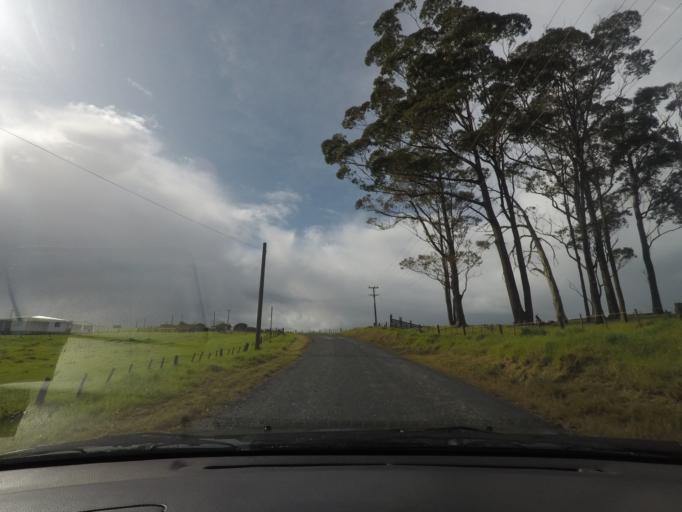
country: NZ
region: Auckland
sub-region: Auckland
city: Warkworth
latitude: -36.4316
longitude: 174.7207
